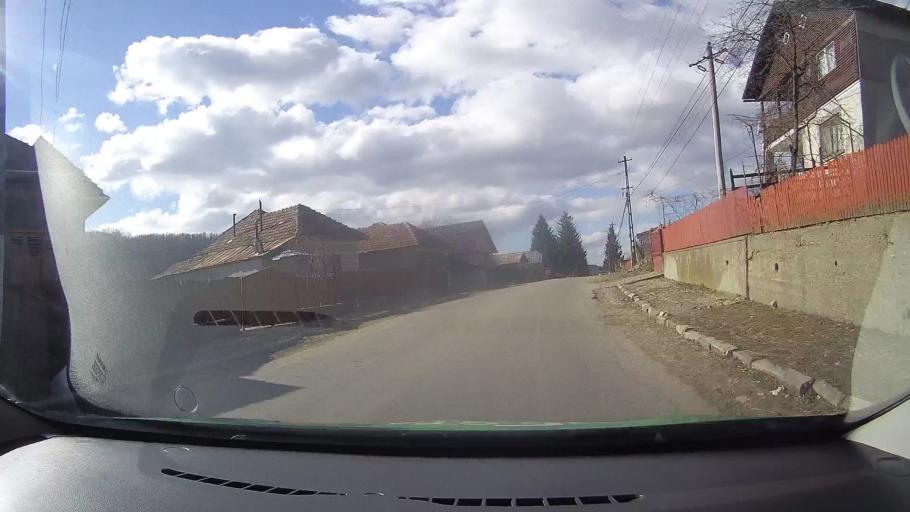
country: RO
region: Dambovita
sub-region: Comuna Bezdead
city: Bezdead
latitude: 45.1485
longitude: 25.5137
